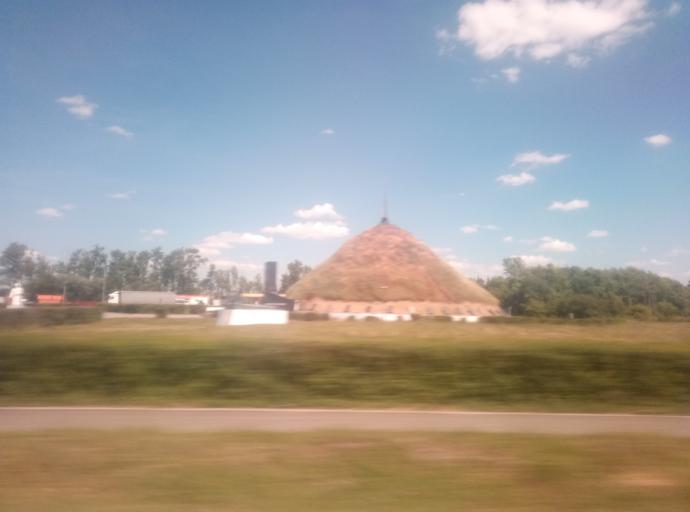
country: RU
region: Tula
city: Kireyevsk
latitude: 54.0192
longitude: 37.9084
